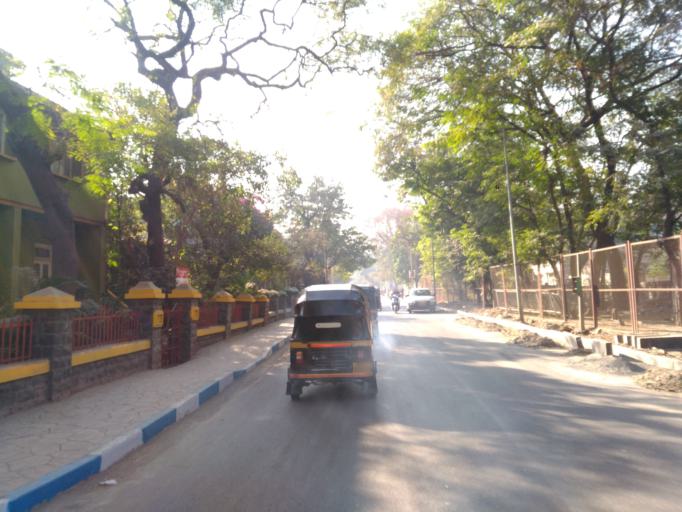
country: IN
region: Maharashtra
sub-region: Pune Division
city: Pune
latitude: 18.5128
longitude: 73.8715
